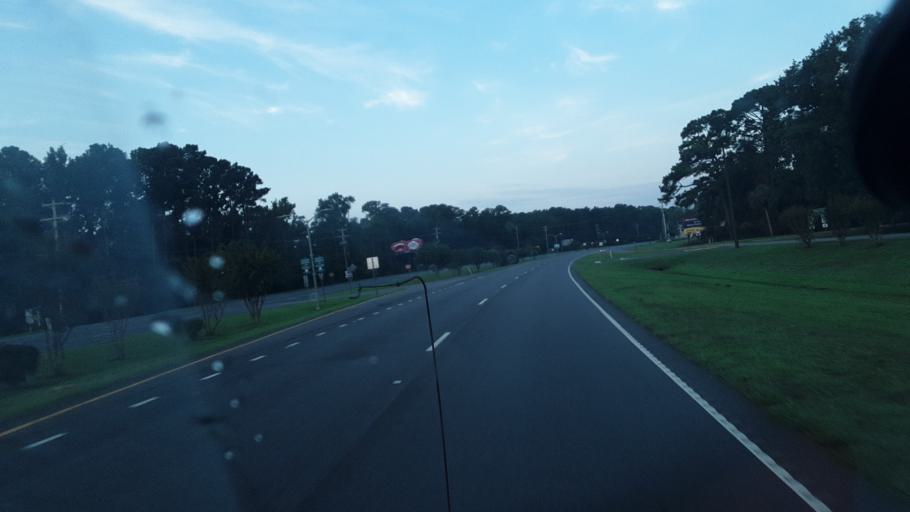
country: US
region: South Carolina
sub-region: Horry County
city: Little River
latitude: 33.8838
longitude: -78.5994
